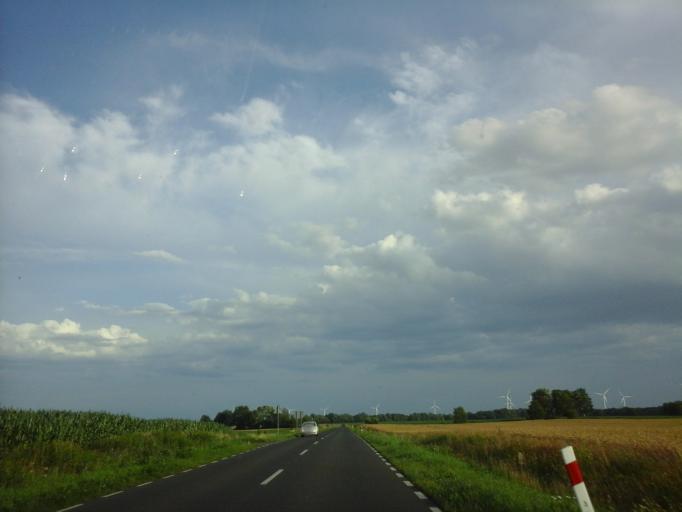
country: PL
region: West Pomeranian Voivodeship
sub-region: Powiat kamienski
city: Kamien Pomorski
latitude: 53.9113
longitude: 14.8508
